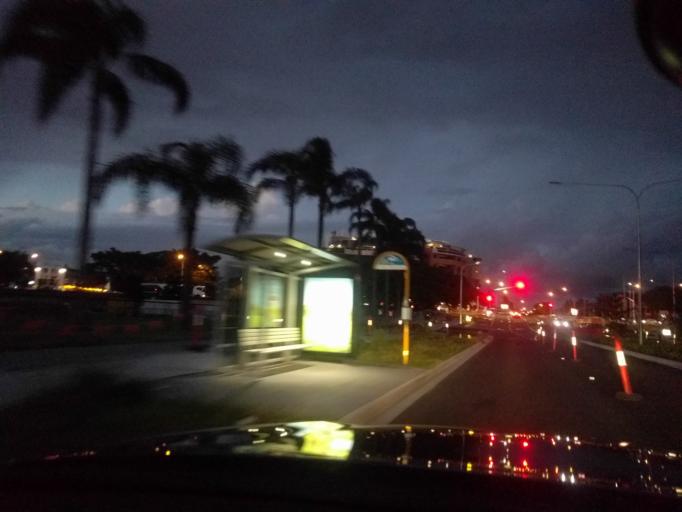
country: AU
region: Queensland
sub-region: Brisbane
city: Ascot
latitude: -27.4390
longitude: 153.0705
